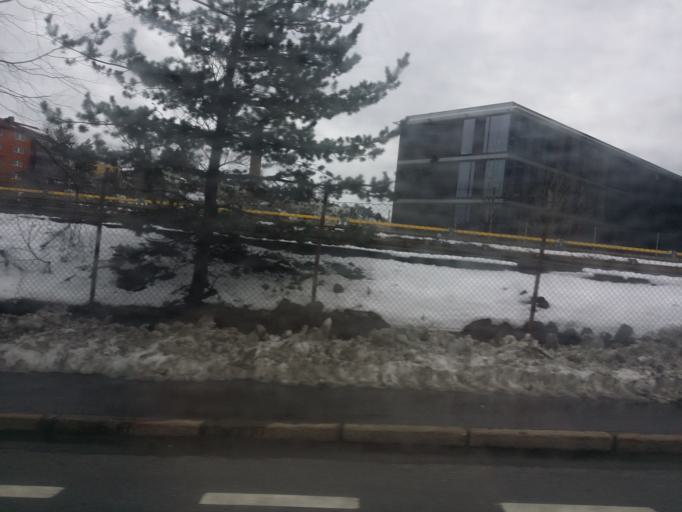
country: NO
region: Oslo
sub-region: Oslo
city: Oslo
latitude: 59.9085
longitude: 10.8159
